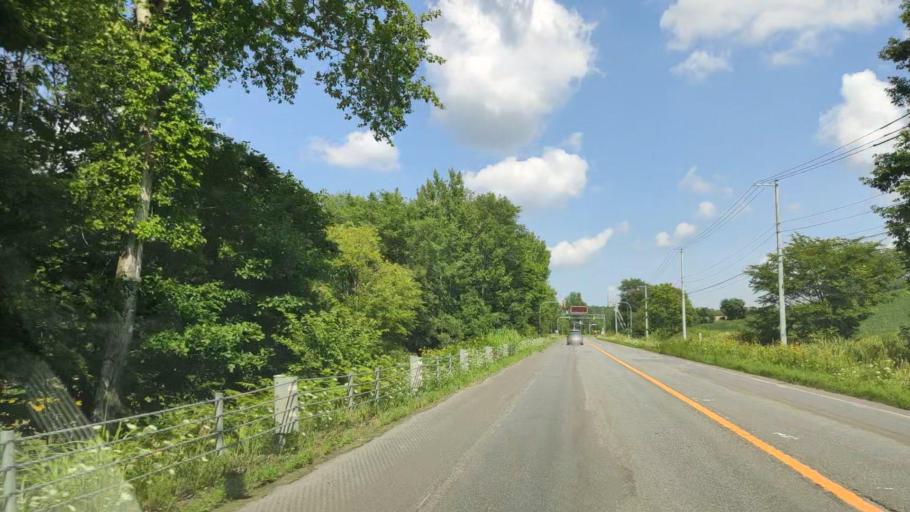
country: JP
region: Hokkaido
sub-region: Asahikawa-shi
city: Asahikawa
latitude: 43.5780
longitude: 142.4389
